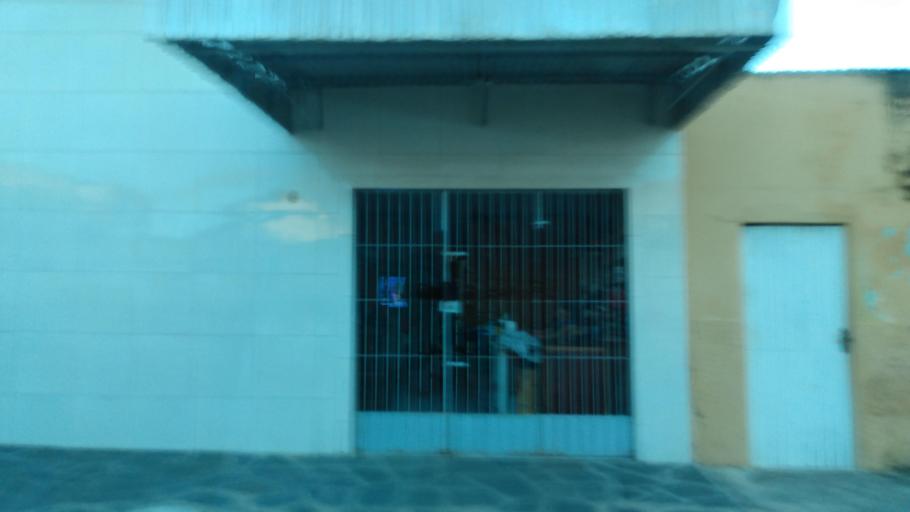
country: BR
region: Pernambuco
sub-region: Bezerros
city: Bezerros
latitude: -8.2407
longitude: -35.7518
